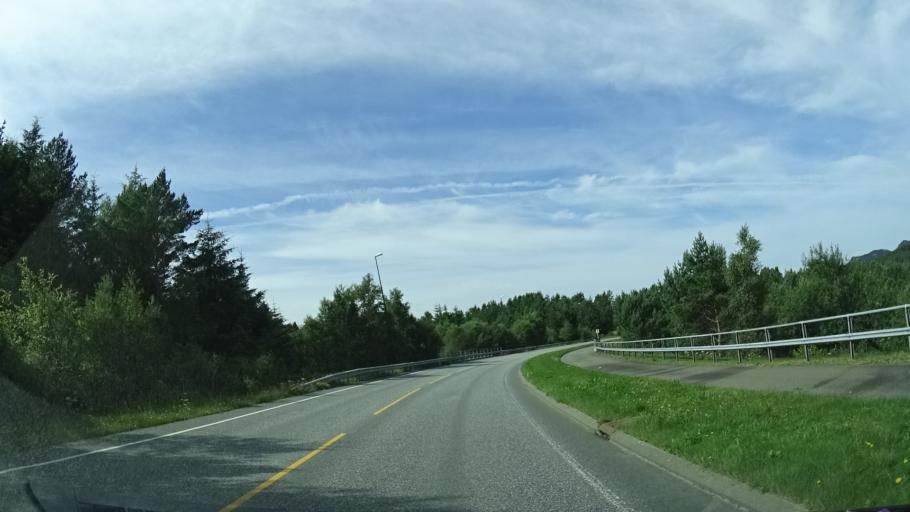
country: NO
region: Hordaland
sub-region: Bomlo
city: Mosterhamn
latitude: 59.7327
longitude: 5.3602
